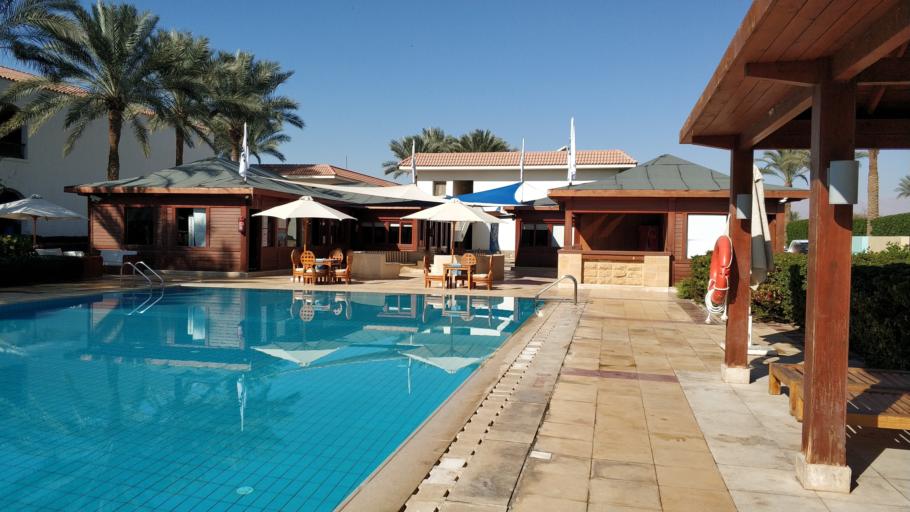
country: EG
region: South Sinai
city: Sharm el-Sheikh
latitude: 27.9208
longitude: 34.3612
